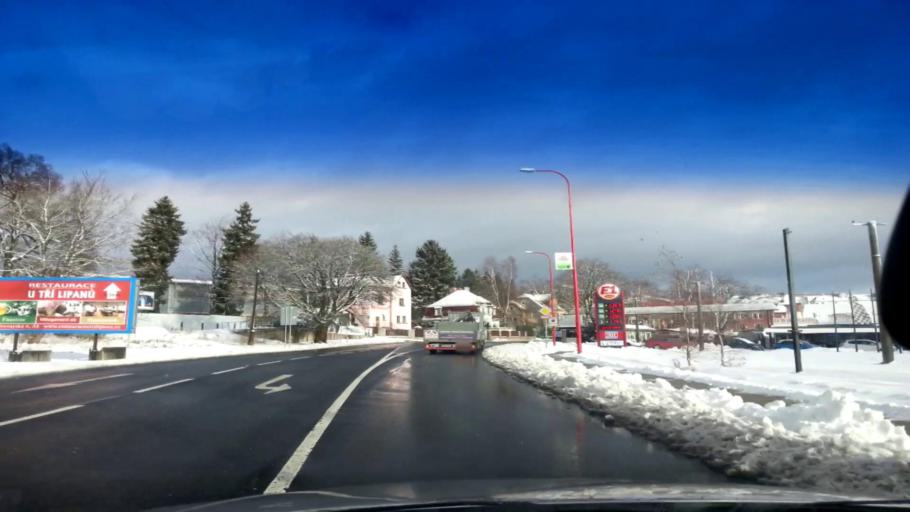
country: CZ
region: Karlovarsky
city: As
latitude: 50.2180
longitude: 12.1758
